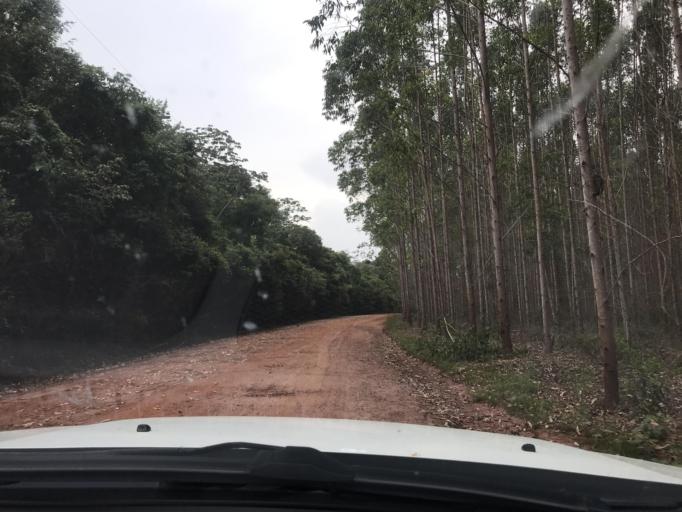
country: BR
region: Bahia
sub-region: Entre Rios
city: Entre Rios
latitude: -12.1055
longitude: -38.1873
